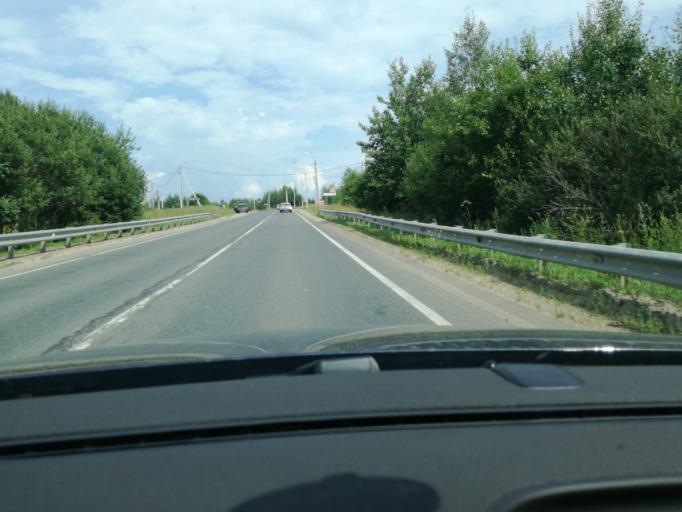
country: RU
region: Moskovskaya
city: Semkhoz
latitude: 56.2765
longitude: 38.0473
